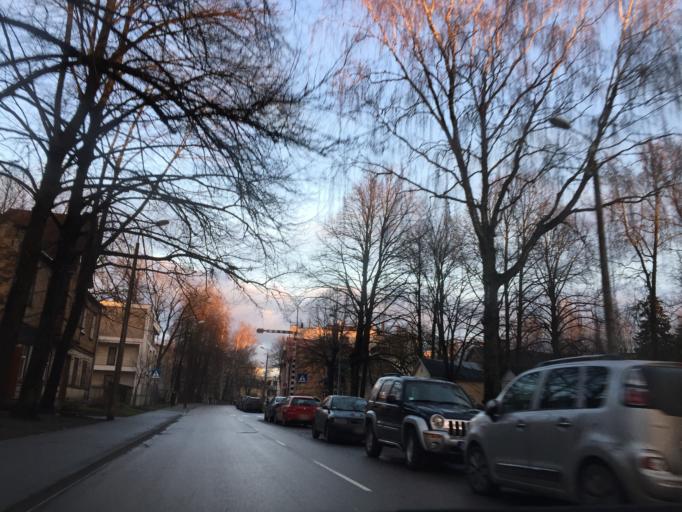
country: LV
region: Marupe
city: Marupe
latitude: 56.9368
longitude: 24.0430
